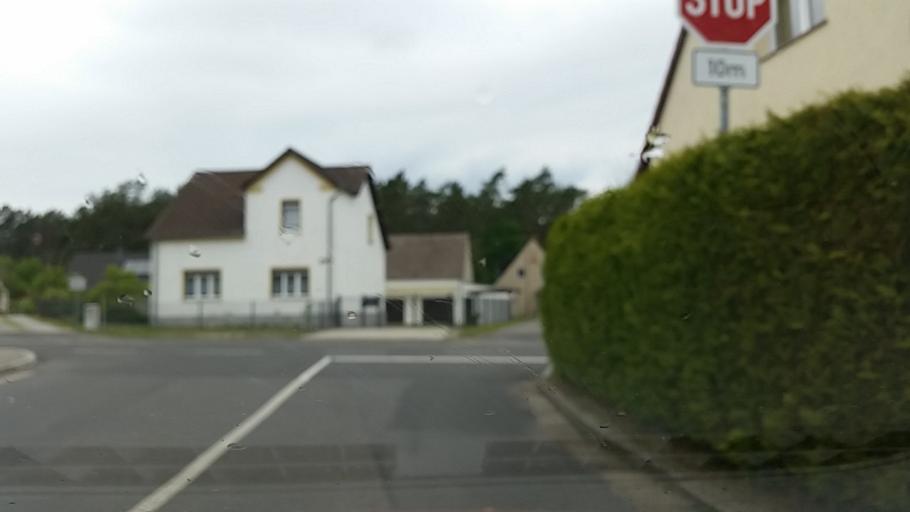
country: DE
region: Brandenburg
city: Reichenwalde
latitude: 52.2911
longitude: 13.9859
